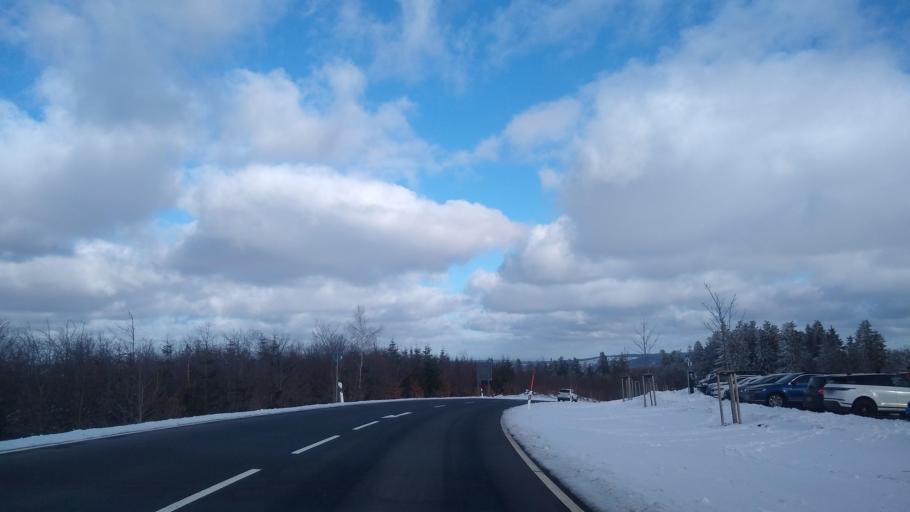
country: DE
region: Hesse
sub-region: Regierungsbezirk Kassel
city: Gersfeld
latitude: 50.5008
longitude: 9.9489
